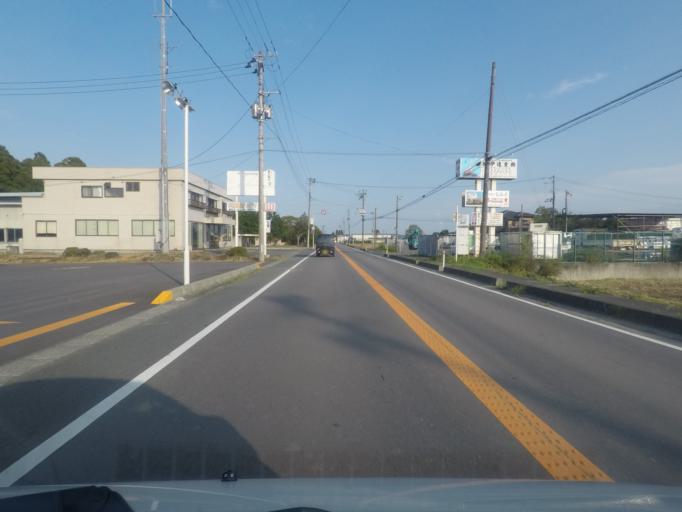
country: JP
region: Fukushima
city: Namie
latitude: 37.4969
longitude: 140.9713
